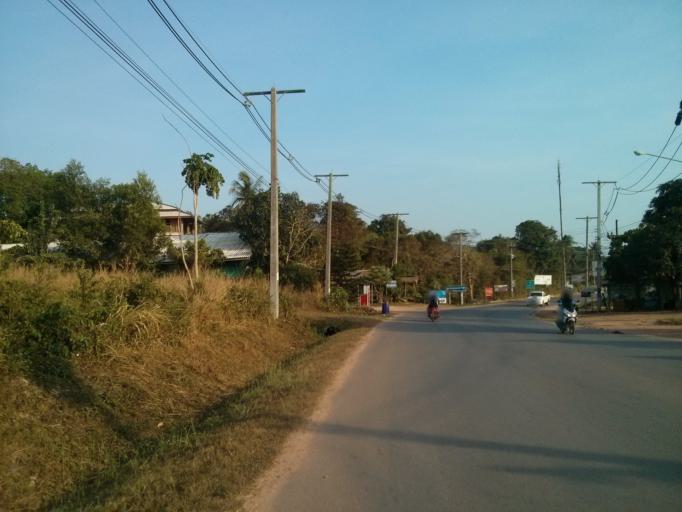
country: TH
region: Krabi
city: Saladan
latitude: 7.5937
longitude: 99.0353
